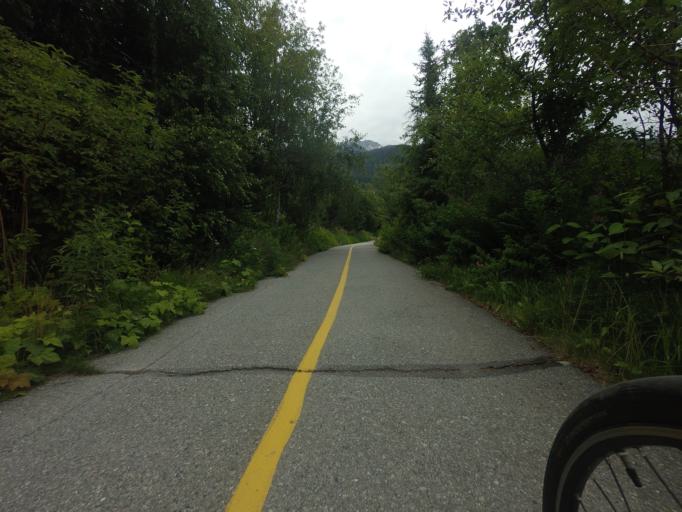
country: CA
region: British Columbia
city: Whistler
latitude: 50.0933
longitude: -123.0000
